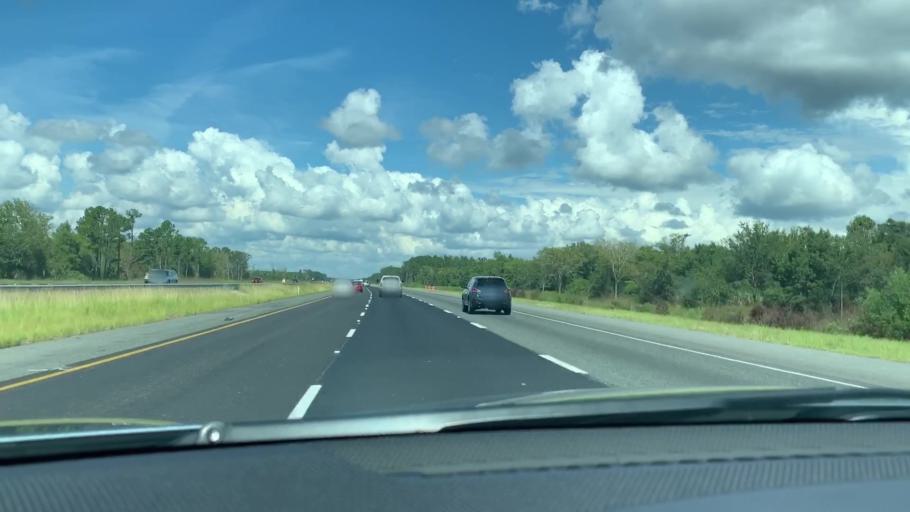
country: US
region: Georgia
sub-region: Camden County
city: Woodbine
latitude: 30.9912
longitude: -81.6653
